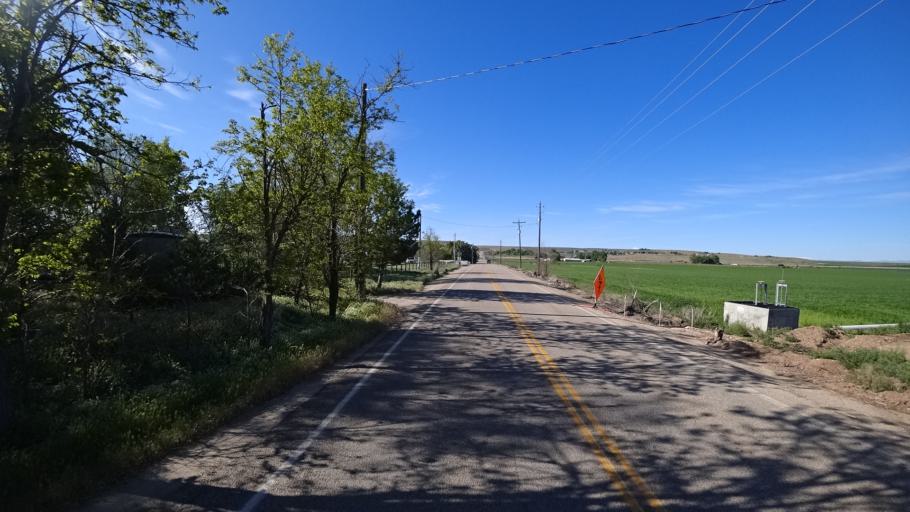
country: US
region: Idaho
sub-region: Ada County
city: Garden City
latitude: 43.5366
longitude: -116.2742
